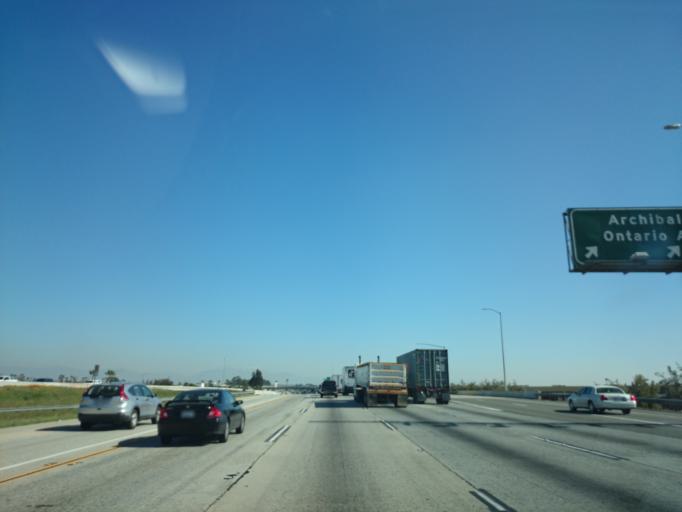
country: US
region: California
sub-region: San Bernardino County
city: Rancho Cucamonga
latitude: 34.0677
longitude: -117.6008
